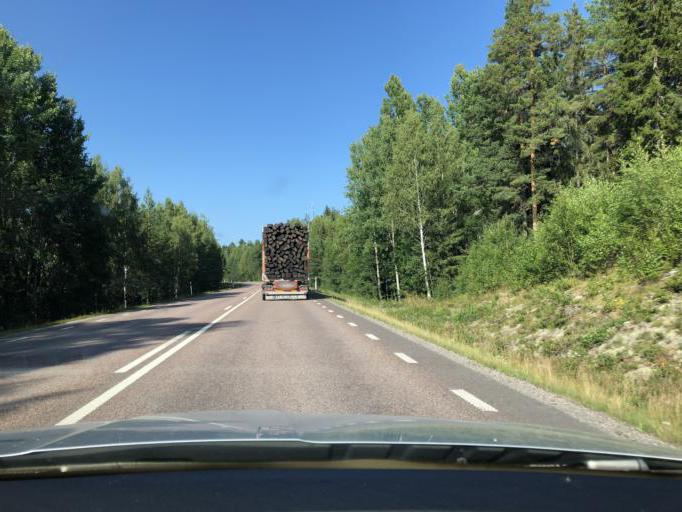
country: SE
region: Dalarna
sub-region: Faluns Kommun
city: Falun
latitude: 60.5785
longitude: 15.7734
